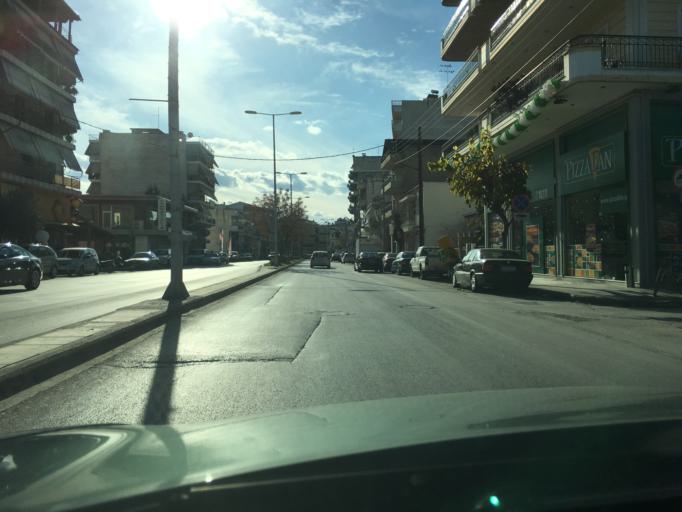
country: GR
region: Thessaly
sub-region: Nomos Larisis
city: Larisa
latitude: 39.6345
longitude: 22.4294
